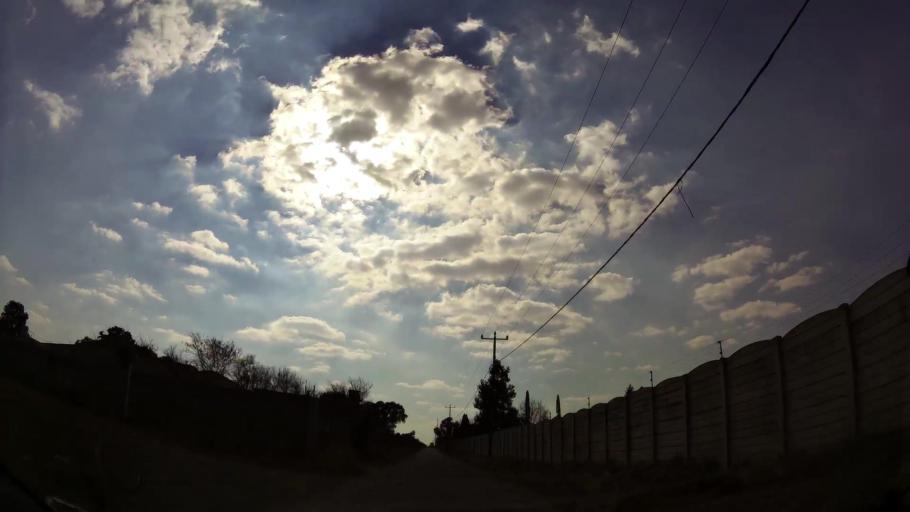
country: ZA
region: Gauteng
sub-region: Ekurhuleni Metropolitan Municipality
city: Benoni
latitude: -26.0918
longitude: 28.3625
